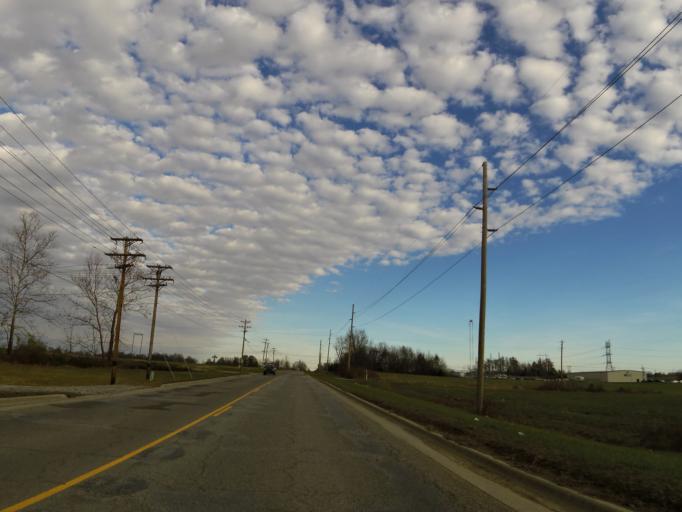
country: US
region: Illinois
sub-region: Jefferson County
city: Mount Vernon
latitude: 38.3285
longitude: -88.9700
